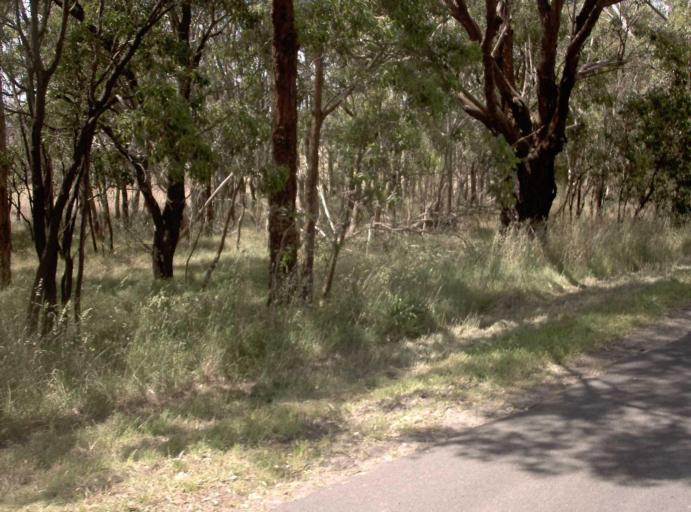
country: AU
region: Victoria
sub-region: Latrobe
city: Traralgon
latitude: -38.1681
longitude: 146.6951
